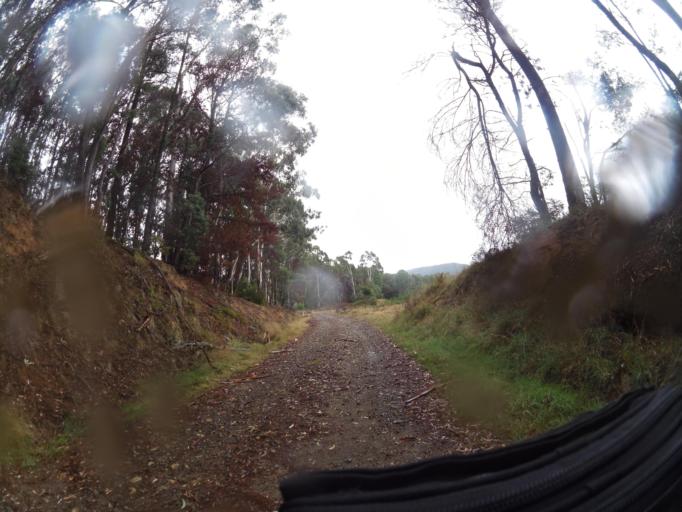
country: AU
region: New South Wales
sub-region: Greater Hume Shire
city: Holbrook
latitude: -36.2246
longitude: 147.5773
